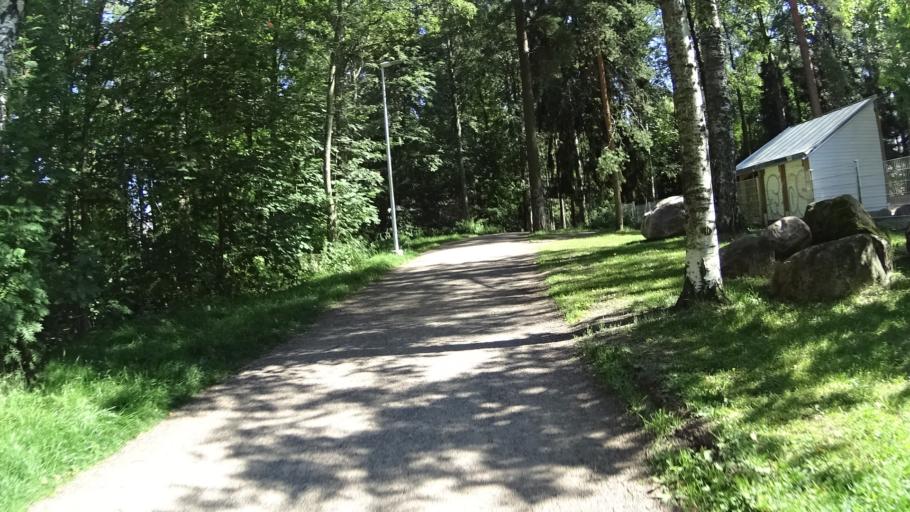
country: FI
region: Uusimaa
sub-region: Helsinki
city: Teekkarikylae
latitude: 60.2401
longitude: 24.8802
